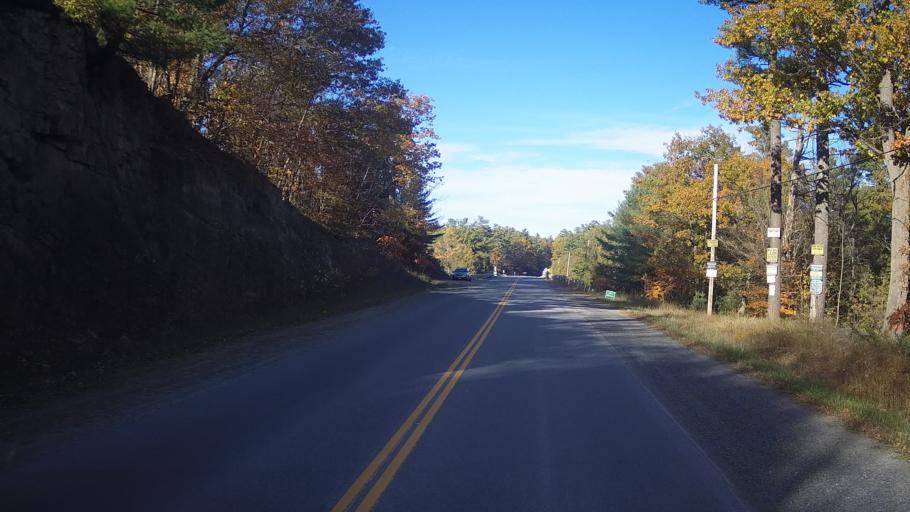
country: CA
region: Ontario
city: Perth
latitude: 44.6038
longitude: -76.4035
